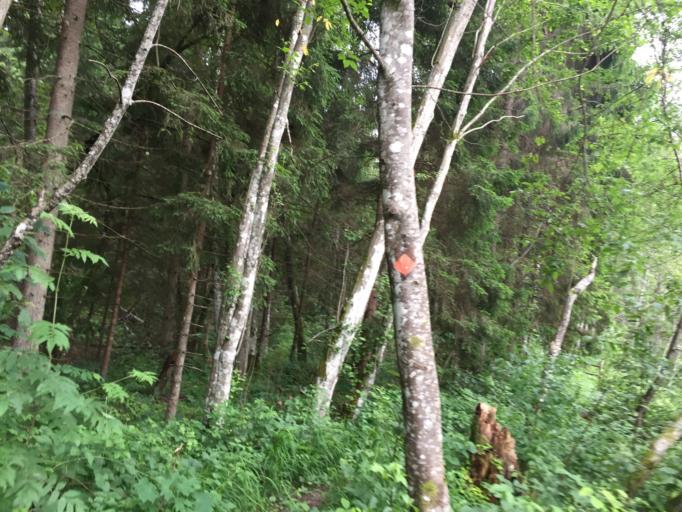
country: LV
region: Ligatne
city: Ligatne
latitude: 57.2352
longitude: 25.1553
